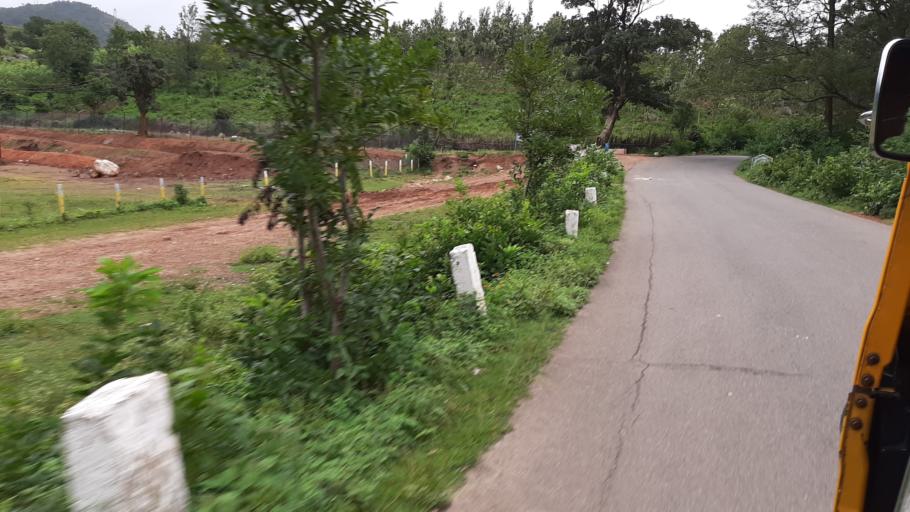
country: IN
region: Andhra Pradesh
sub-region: Vizianagaram District
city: Salur
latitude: 18.2417
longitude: 82.9992
